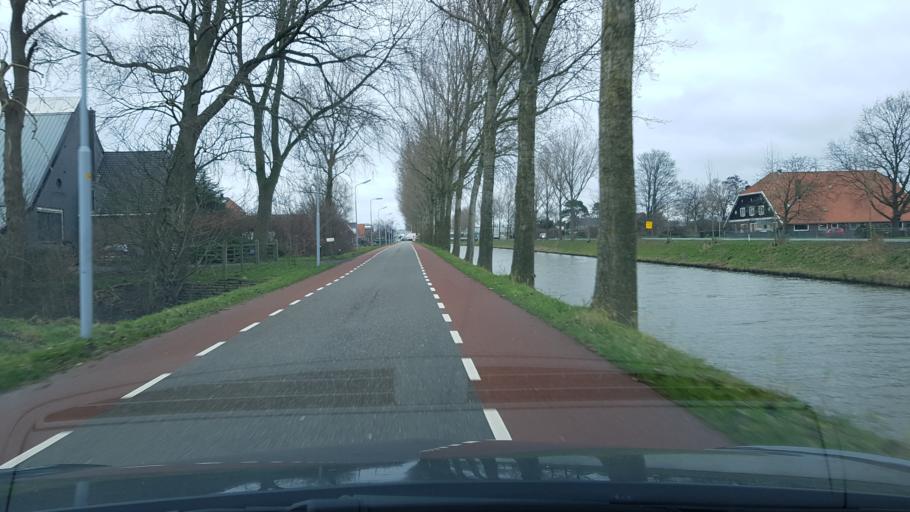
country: NL
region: North Holland
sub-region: Gemeente Haarlemmermeer
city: Hoofddorp
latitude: 52.3439
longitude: 4.7474
